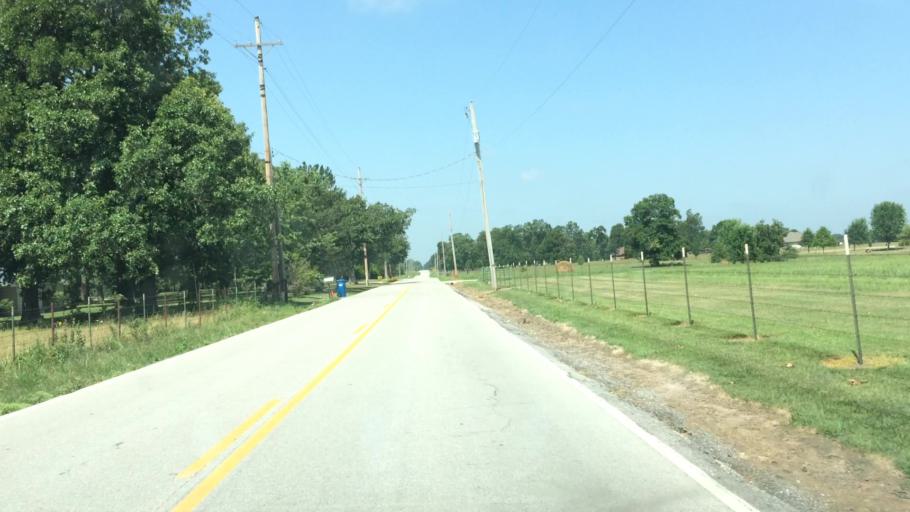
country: US
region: Missouri
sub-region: Greene County
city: Strafford
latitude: 37.2714
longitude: -93.1617
